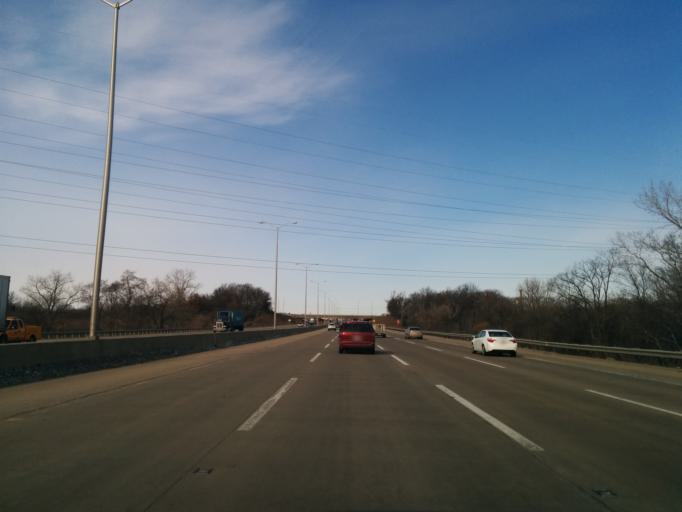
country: US
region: Illinois
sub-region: Lake County
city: Gurnee
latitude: 42.3543
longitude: -87.9315
